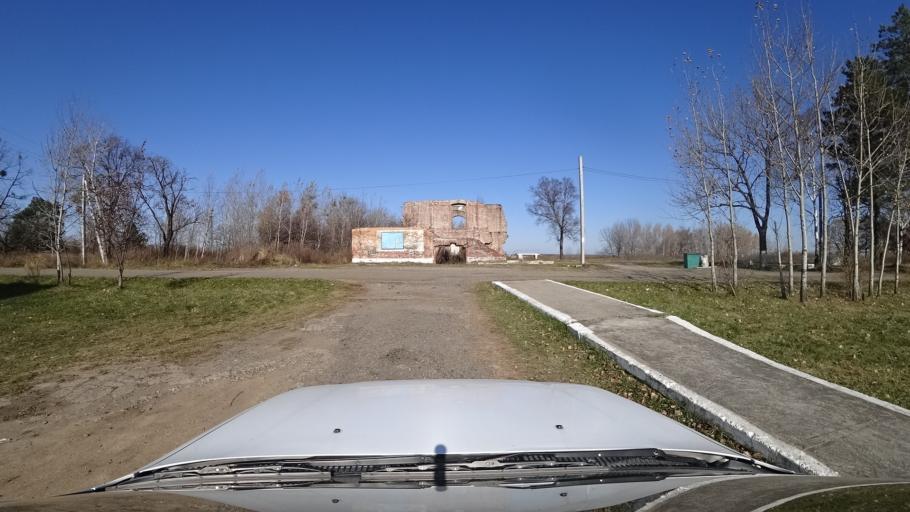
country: RU
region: Primorskiy
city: Dal'nerechensk
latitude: 45.9455
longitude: 133.6866
